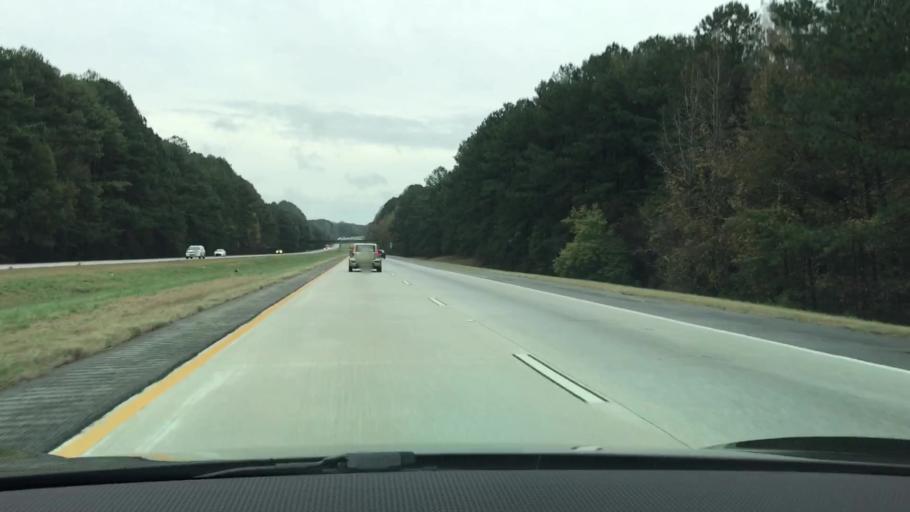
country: US
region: Georgia
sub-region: Greene County
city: Union Point
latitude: 33.5494
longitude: -83.0506
